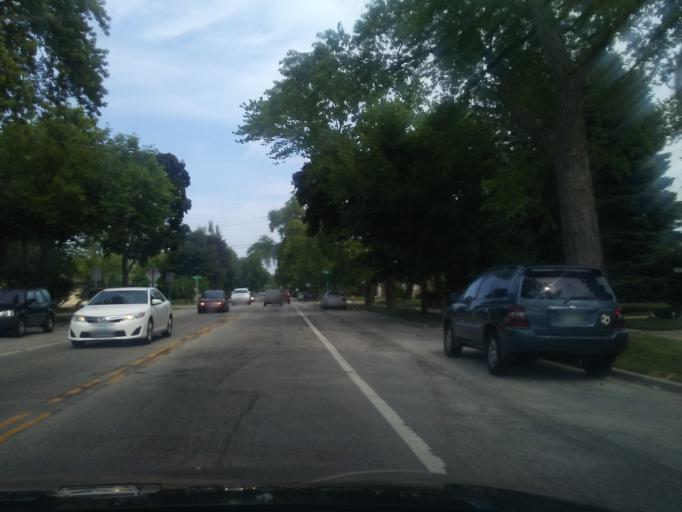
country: US
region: Illinois
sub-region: Cook County
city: Skokie
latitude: 42.0190
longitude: -87.7424
